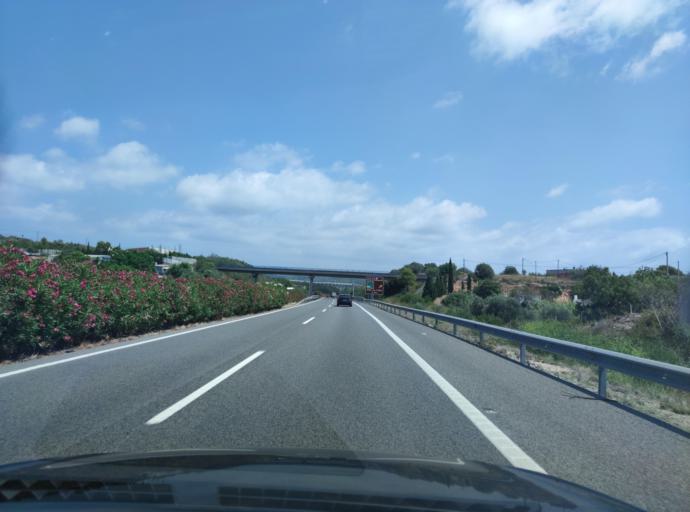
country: ES
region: Catalonia
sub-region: Provincia de Tarragona
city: Amposta
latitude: 40.7169
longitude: 0.5602
